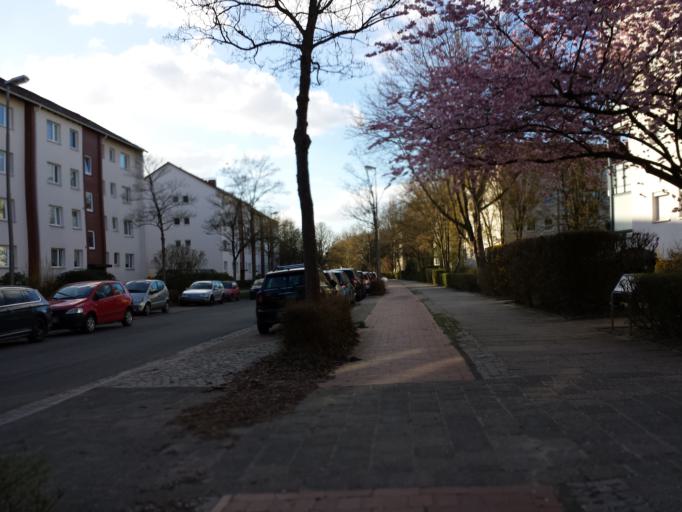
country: DE
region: Bremen
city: Bremen
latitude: 53.0959
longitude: 8.8483
